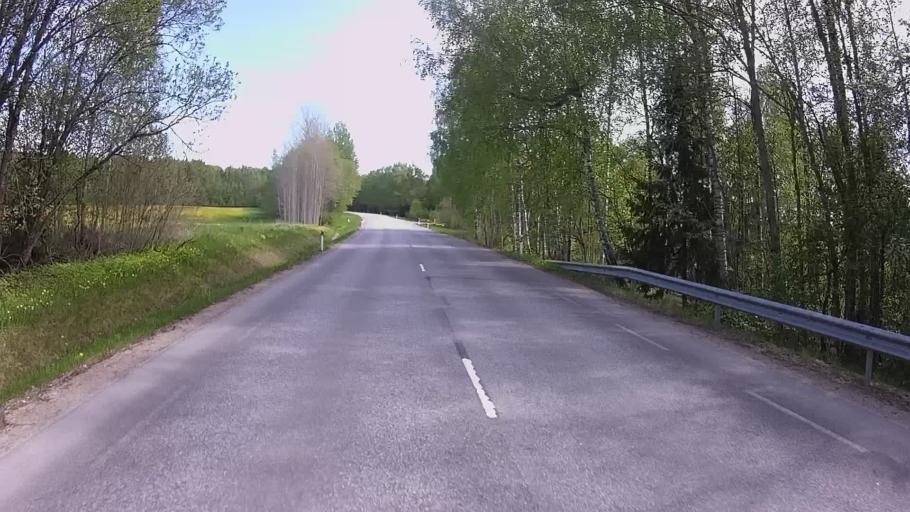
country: EE
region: Valgamaa
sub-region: Valga linn
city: Valga
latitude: 57.7323
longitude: 26.1533
